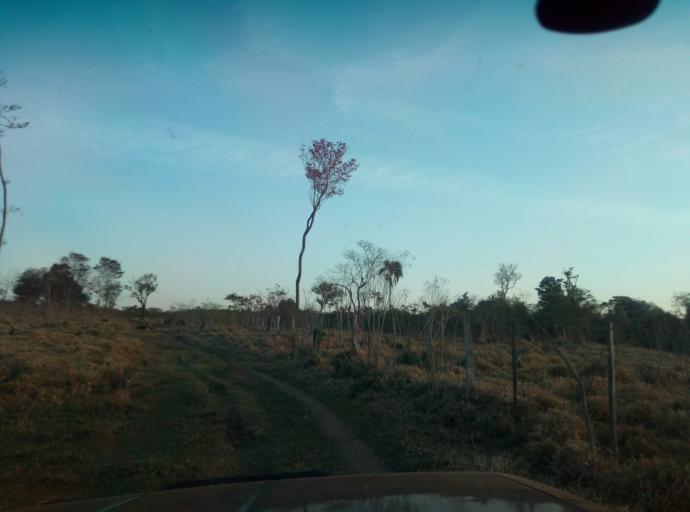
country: PY
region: Caaguazu
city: Yhu
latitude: -25.2017
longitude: -56.1082
